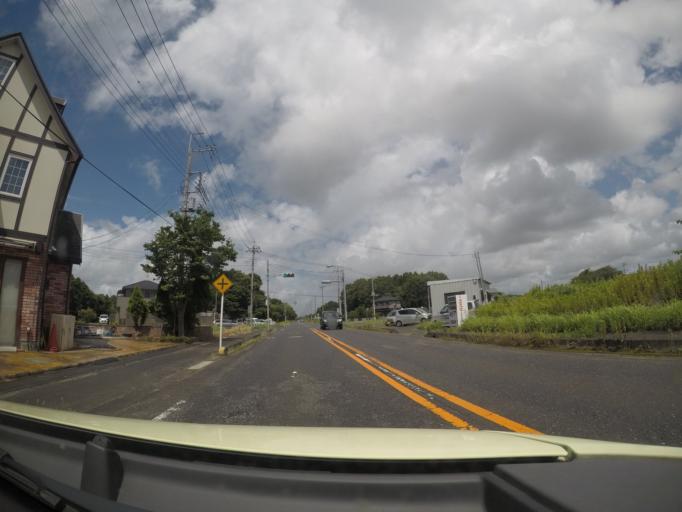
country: JP
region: Ibaraki
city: Ishige
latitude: 36.0757
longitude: 140.0282
